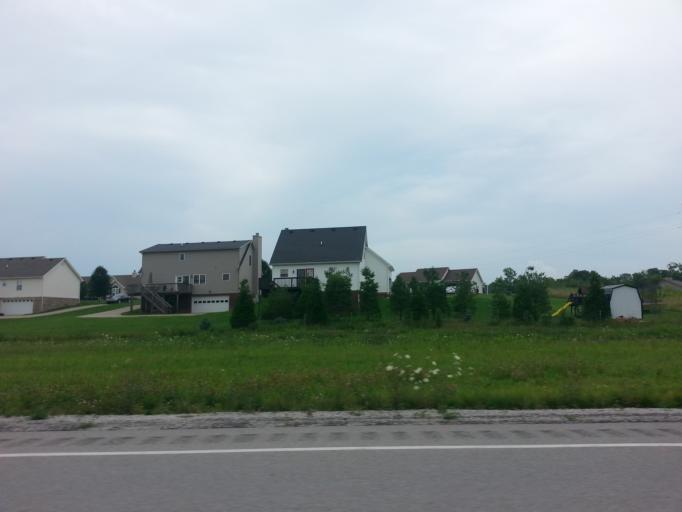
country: US
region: Ohio
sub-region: Brown County
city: Aberdeen
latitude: 38.6063
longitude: -83.8289
